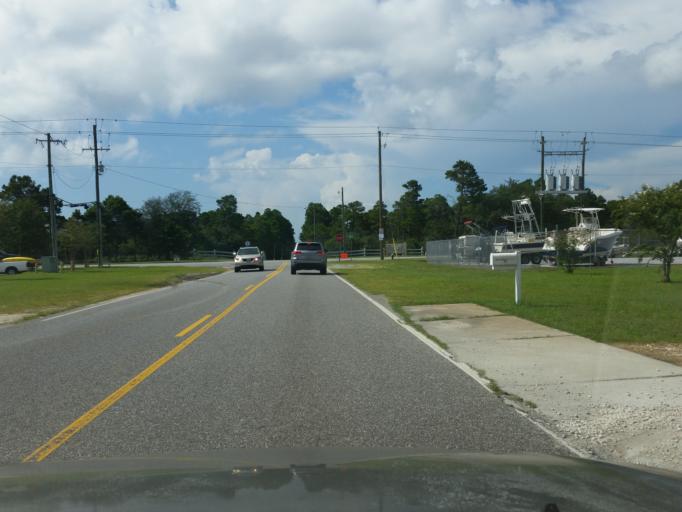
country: US
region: Florida
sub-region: Escambia County
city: Myrtle Grove
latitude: 30.3226
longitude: -87.4038
